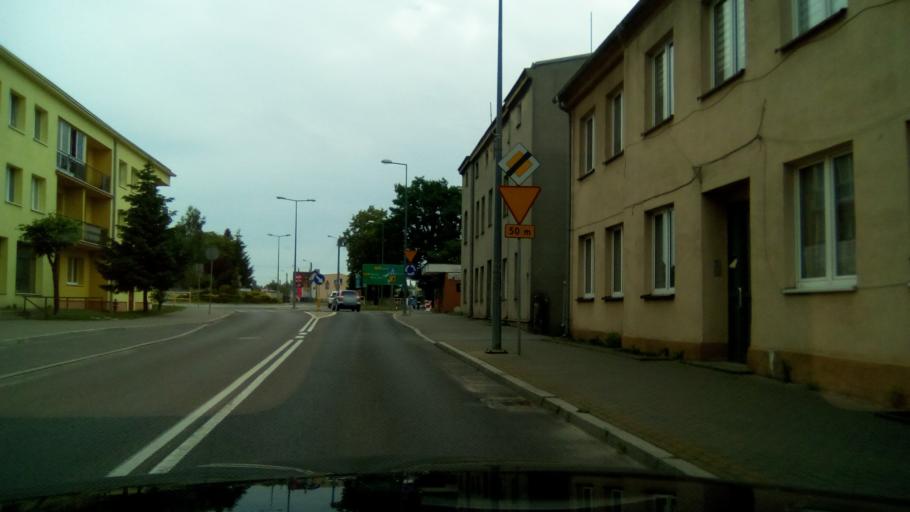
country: PL
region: Kujawsko-Pomorskie
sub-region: Powiat sepolenski
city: Wiecbork
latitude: 53.3565
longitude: 17.4877
